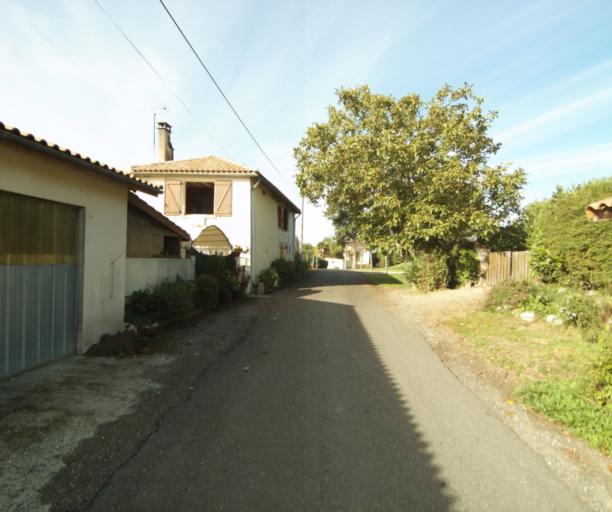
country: FR
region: Midi-Pyrenees
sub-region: Departement du Gers
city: Eauze
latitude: 43.8857
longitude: 0.1391
